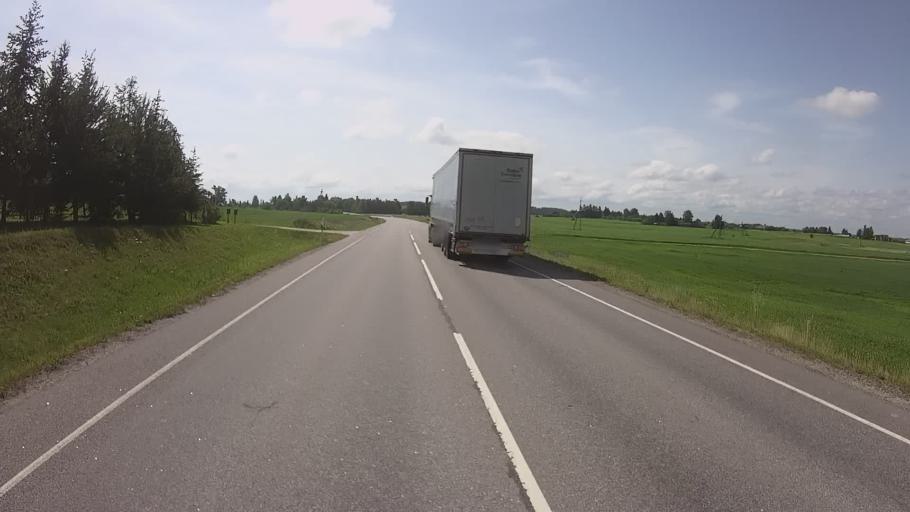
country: EE
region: Tartu
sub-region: UElenurme vald
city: Ulenurme
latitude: 58.2456
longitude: 26.7848
